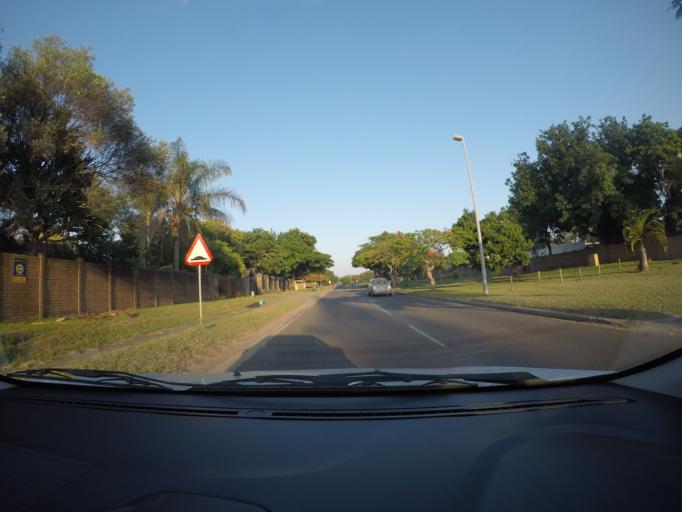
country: ZA
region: KwaZulu-Natal
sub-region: uThungulu District Municipality
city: Richards Bay
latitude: -28.7767
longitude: 32.1040
